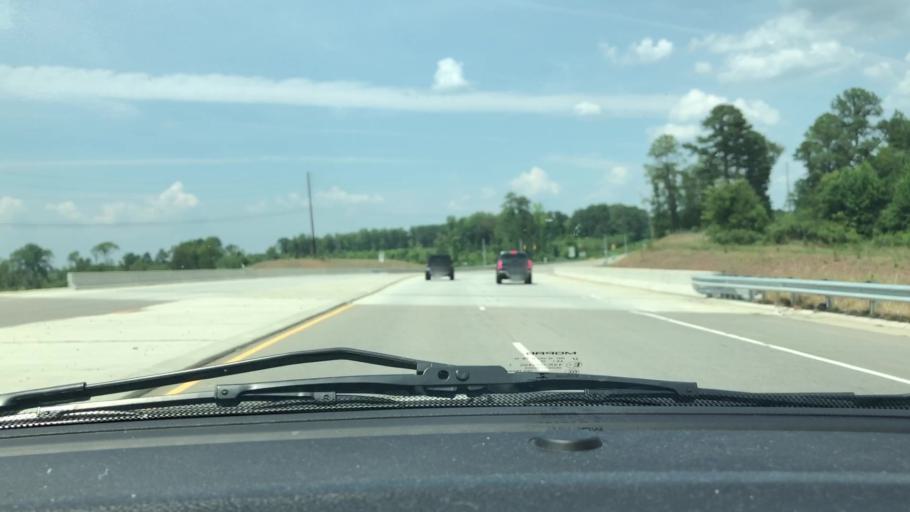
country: US
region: North Carolina
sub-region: Chatham County
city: Farmville
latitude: 35.5400
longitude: -79.2406
